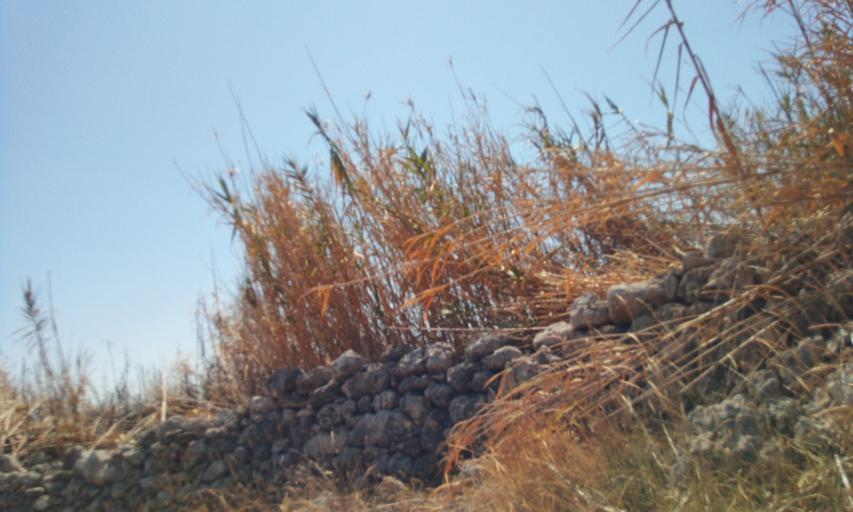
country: IT
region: Apulia
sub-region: Provincia di Bari
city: Polignano a Mare
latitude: 40.9828
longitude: 17.2515
